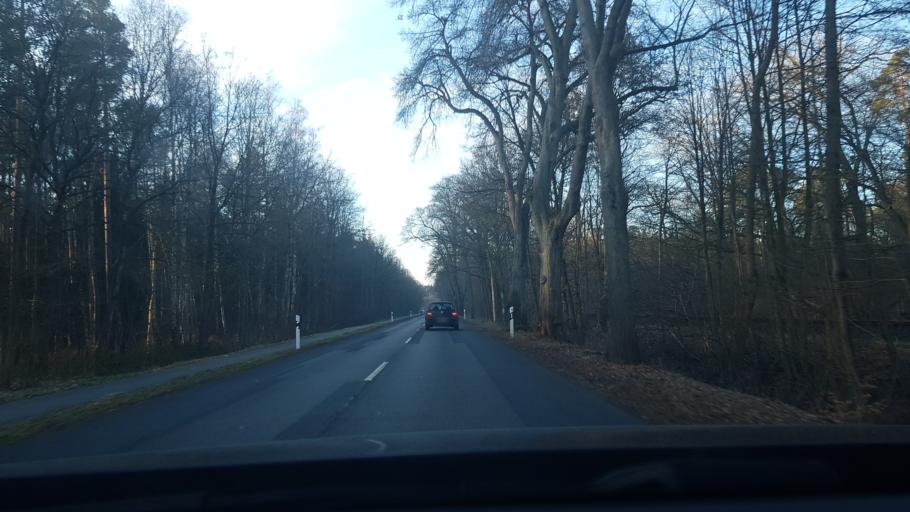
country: DE
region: Lower Saxony
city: Gifhorn
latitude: 52.5017
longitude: 10.5732
